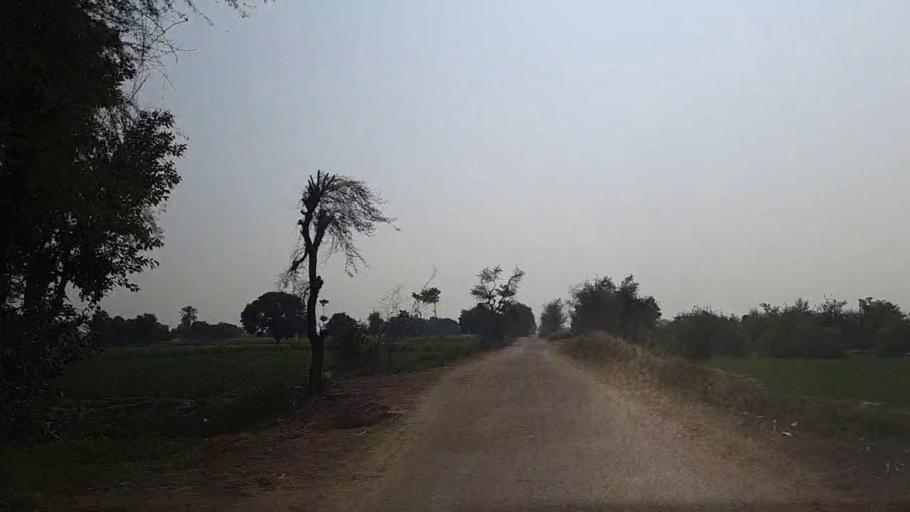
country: PK
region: Sindh
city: Jam Sahib
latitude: 26.4615
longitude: 68.5236
